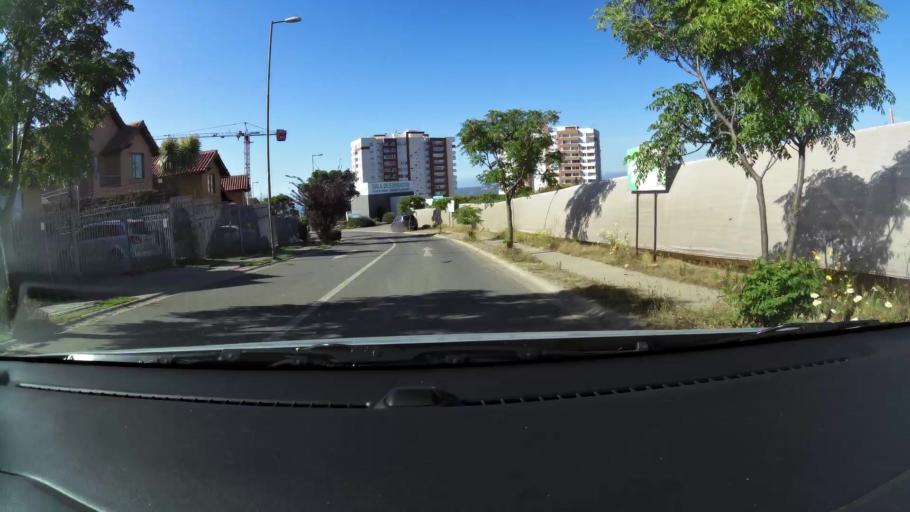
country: CL
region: Valparaiso
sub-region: Provincia de Valparaiso
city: Vina del Mar
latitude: -33.0404
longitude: -71.5558
